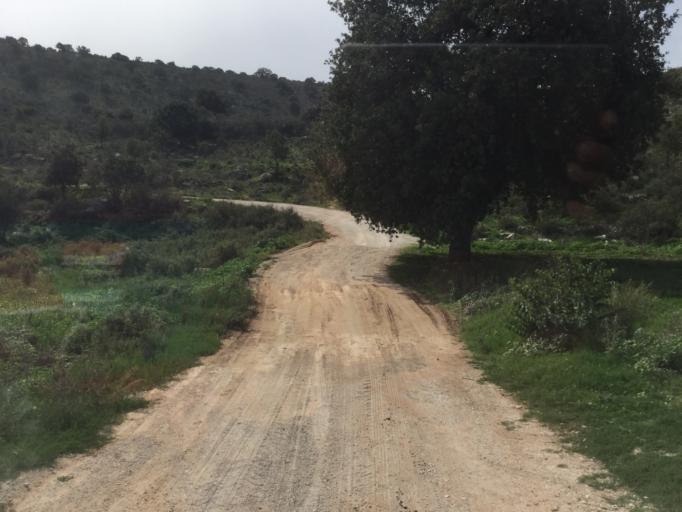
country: GR
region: West Greece
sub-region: Nomos Achaias
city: Lapas
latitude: 38.1832
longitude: 21.3806
